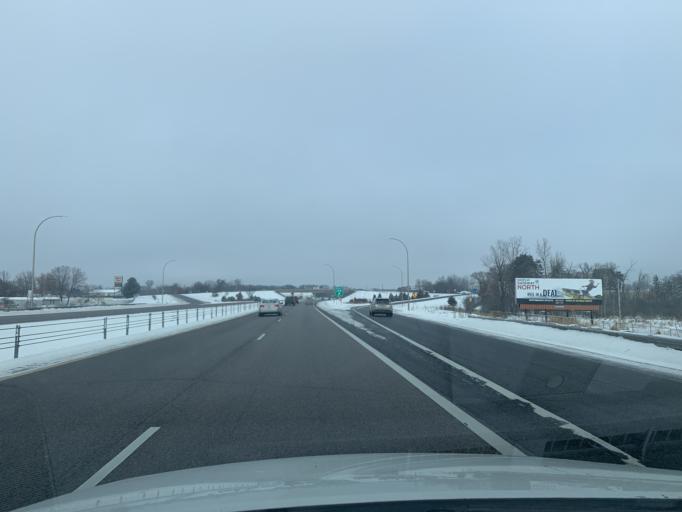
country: US
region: Minnesota
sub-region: Chisago County
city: Stacy
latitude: 45.3934
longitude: -92.9939
